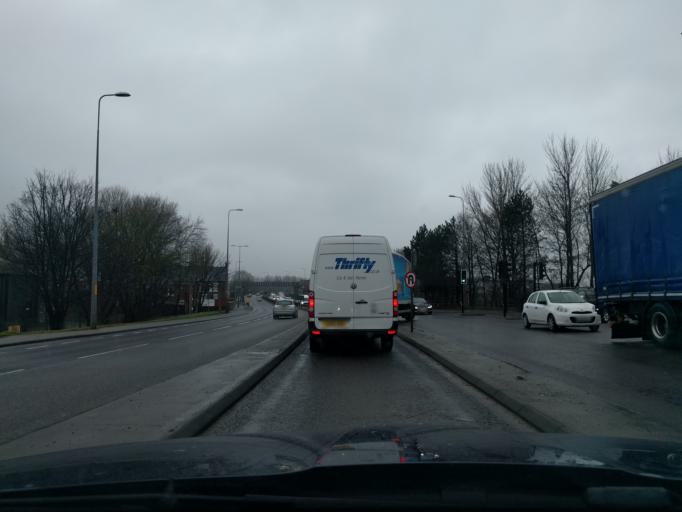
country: GB
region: England
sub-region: Gateshead
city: Felling
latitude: 54.9549
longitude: -1.5643
